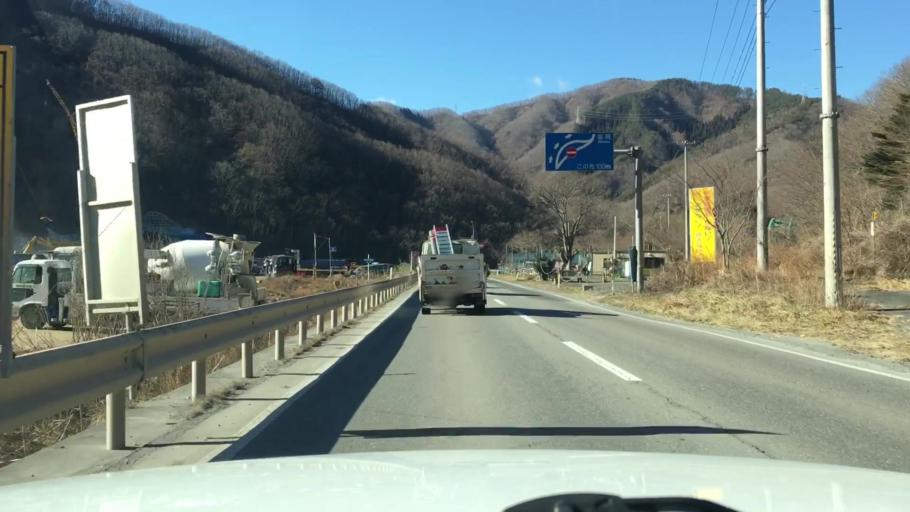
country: JP
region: Iwate
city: Miyako
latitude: 39.6233
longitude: 141.8255
